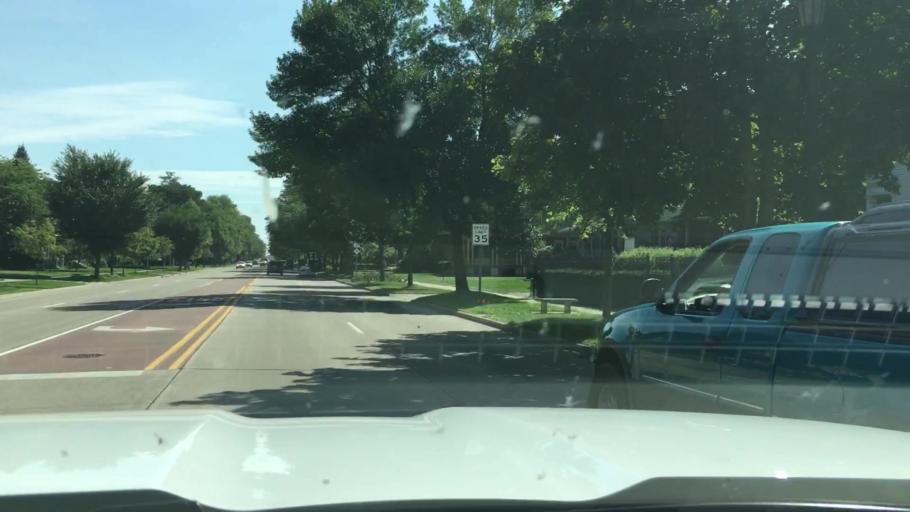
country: US
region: Michigan
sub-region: Bay County
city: Bay City
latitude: 43.5967
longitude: -83.8713
